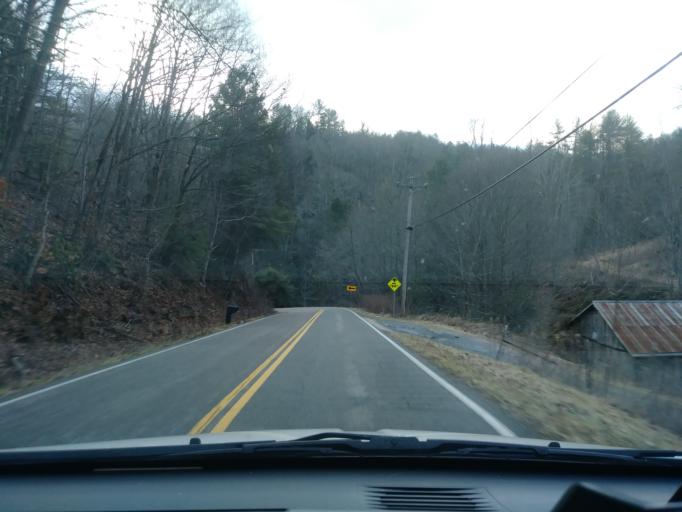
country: US
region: Tennessee
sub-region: Carter County
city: Elizabethton
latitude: 36.2144
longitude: -82.2131
